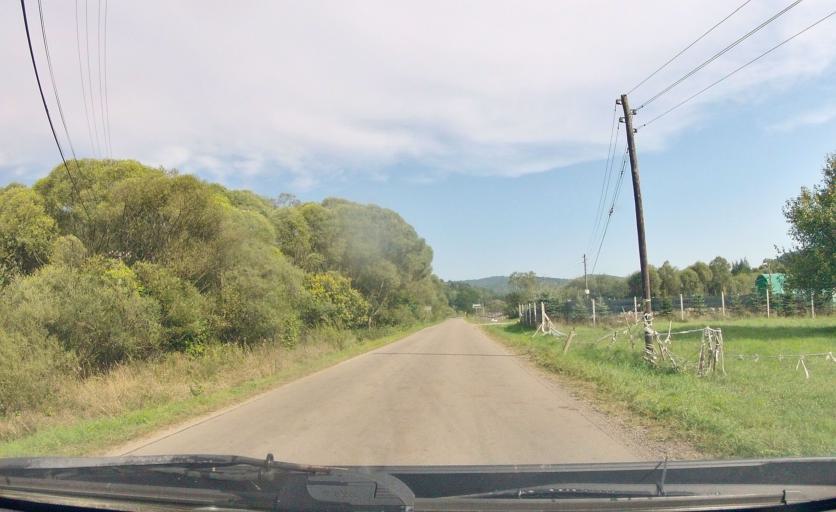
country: PL
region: Subcarpathian Voivodeship
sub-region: Powiat jasielski
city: Krempna
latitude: 49.4992
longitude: 21.5497
